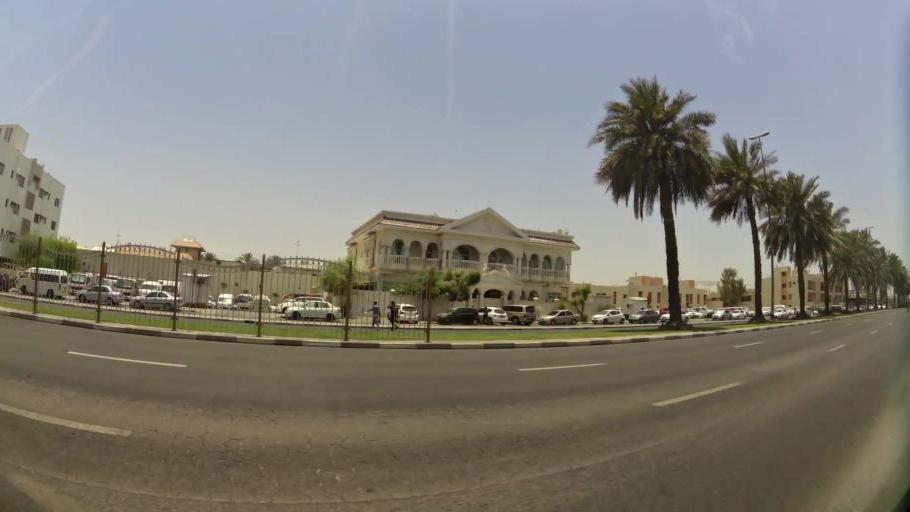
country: AE
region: Ash Shariqah
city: Sharjah
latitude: 25.2778
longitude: 55.3212
